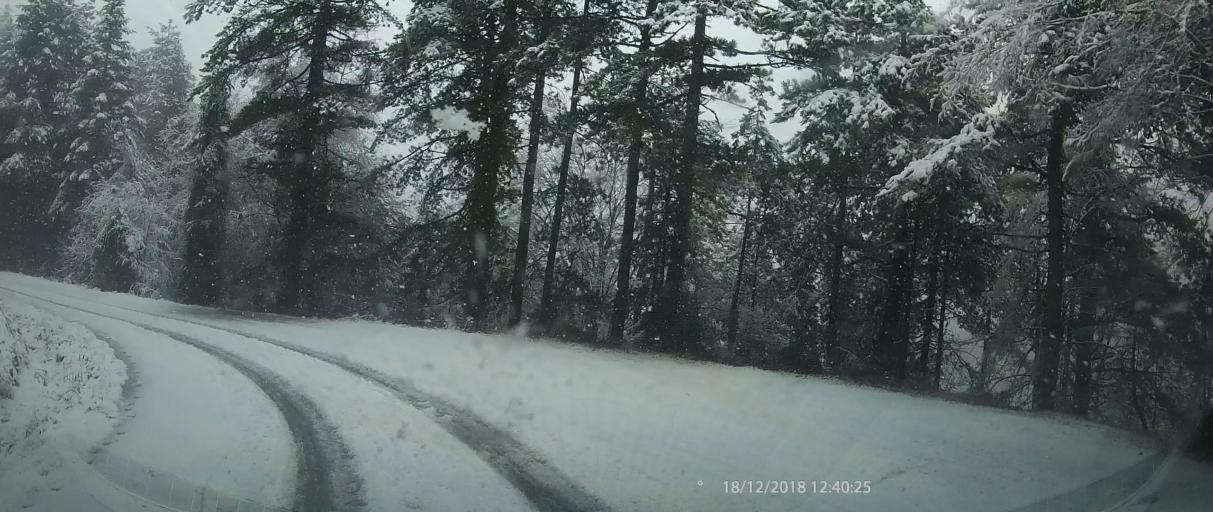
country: GR
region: Central Macedonia
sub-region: Nomos Pierias
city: Litochoro
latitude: 40.0916
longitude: 22.4186
